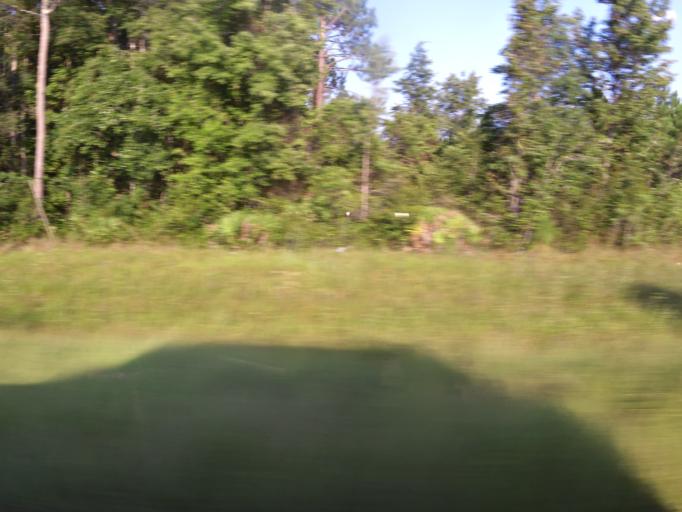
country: US
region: Florida
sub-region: Duval County
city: Baldwin
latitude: 30.3592
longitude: -82.0095
